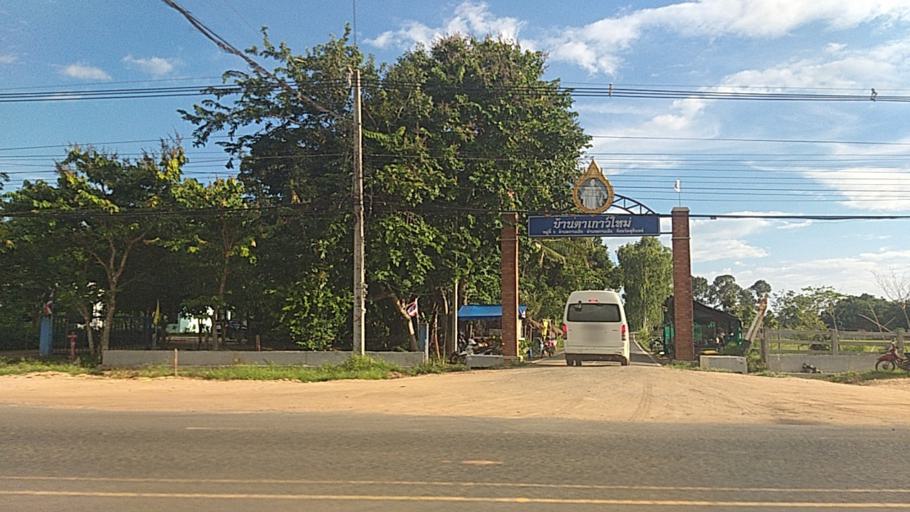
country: TH
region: Surin
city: Kap Choeng
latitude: 14.4770
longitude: 103.5903
